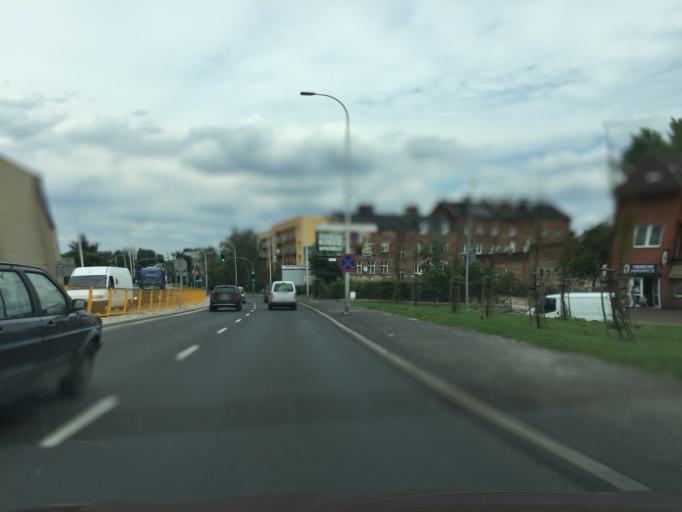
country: PL
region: Greater Poland Voivodeship
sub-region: Kalisz
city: Kalisz
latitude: 51.7600
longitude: 18.0772
